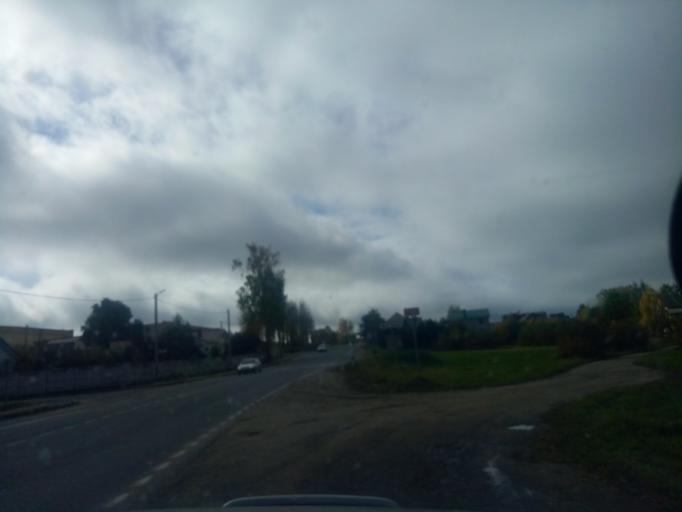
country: BY
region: Minsk
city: Zaslawye
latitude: 53.9985
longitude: 27.2775
